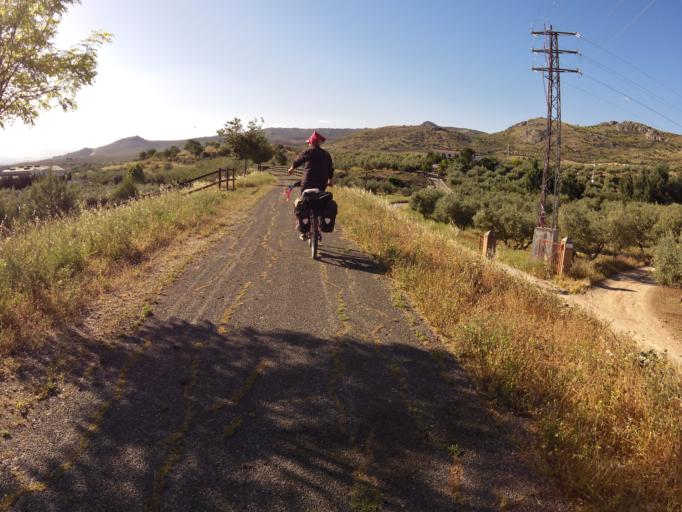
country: ES
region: Andalusia
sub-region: Province of Cordoba
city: Luque
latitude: 37.5704
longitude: -4.2550
